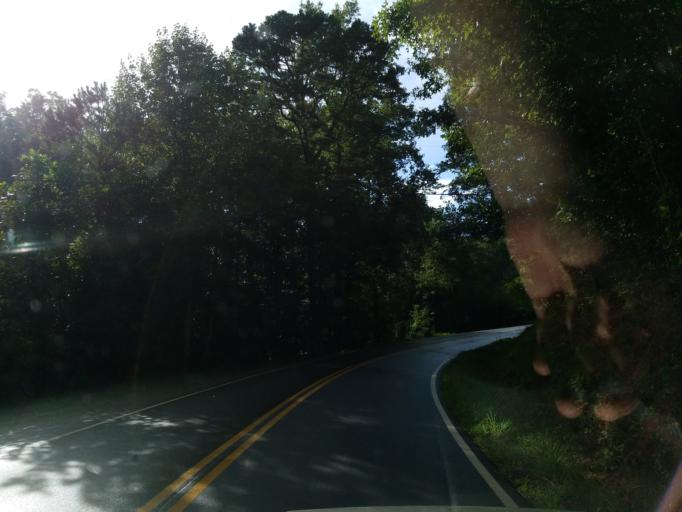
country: US
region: Georgia
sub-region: White County
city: Cleveland
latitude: 34.6238
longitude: -83.8658
